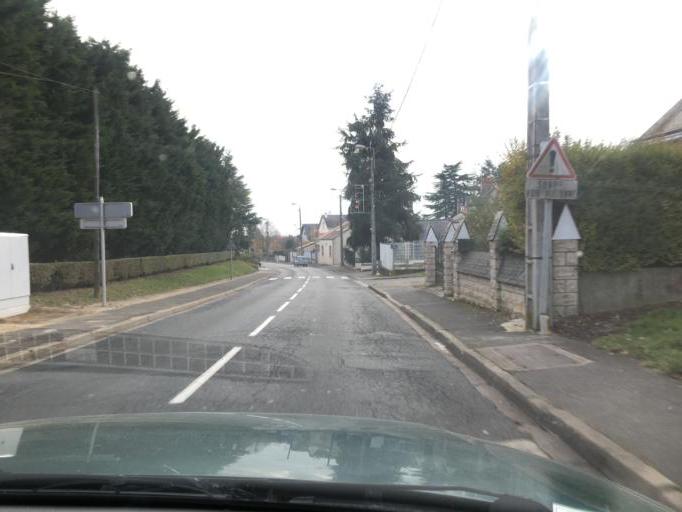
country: FR
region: Centre
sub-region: Departement du Loiret
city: Saran
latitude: 47.9546
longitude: 1.8787
